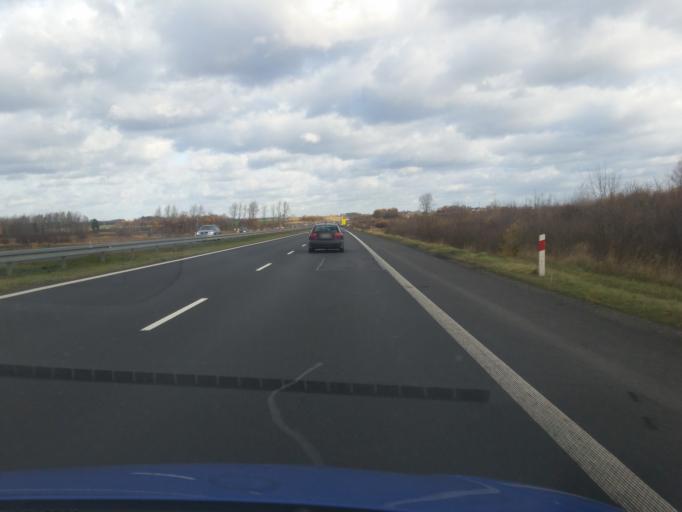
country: PL
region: Silesian Voivodeship
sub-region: Powiat czestochowski
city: Mykanow
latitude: 50.9364
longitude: 19.2333
